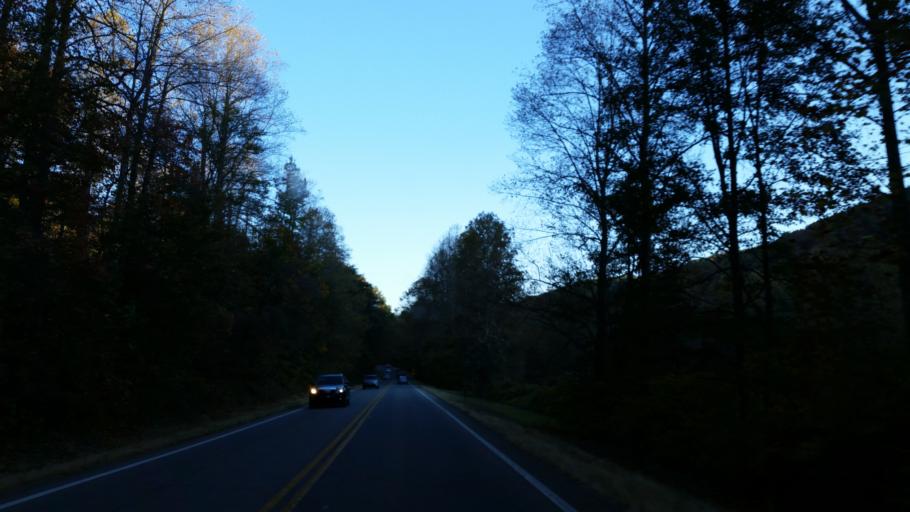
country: US
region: Georgia
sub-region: Pickens County
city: Jasper
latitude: 34.5569
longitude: -84.2962
